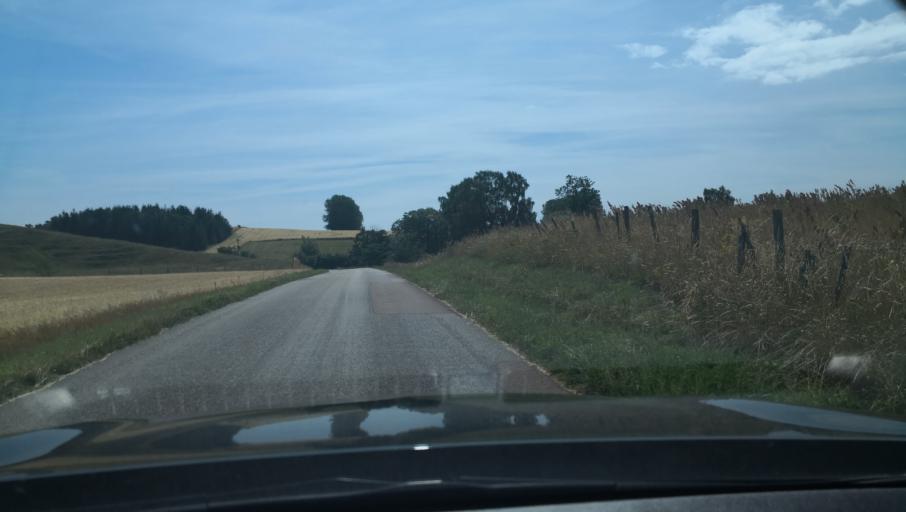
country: SE
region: Skane
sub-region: Ystads Kommun
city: Kopingebro
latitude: 55.3934
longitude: 14.1381
